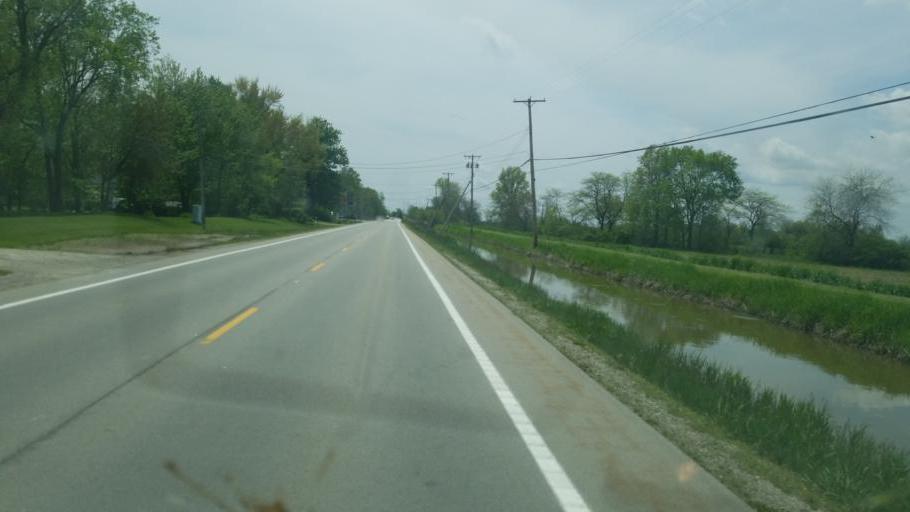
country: US
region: Ohio
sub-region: Ottawa County
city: Oak Harbor
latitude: 41.4597
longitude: -83.0504
